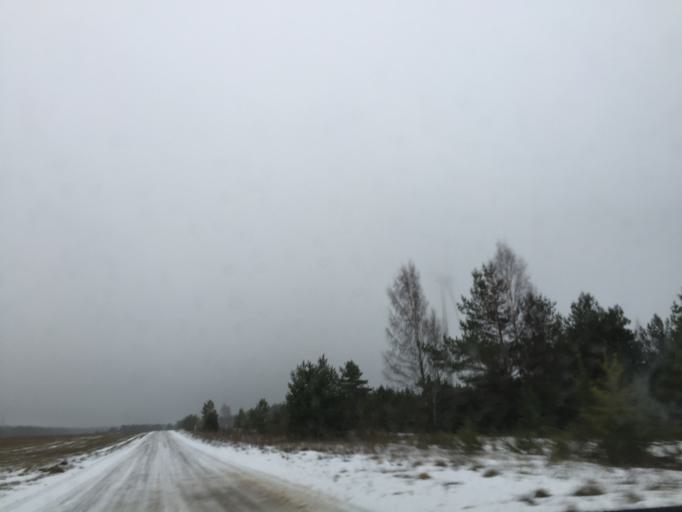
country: EE
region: Laeaene
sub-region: Lihula vald
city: Lihula
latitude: 58.6255
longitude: 23.5385
